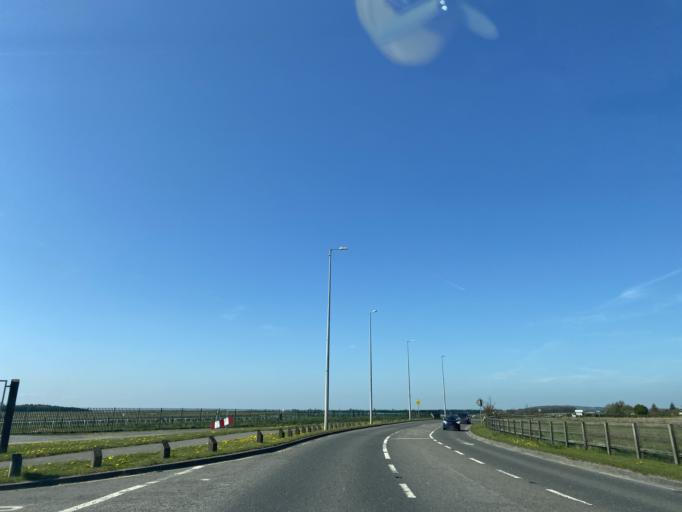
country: IE
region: Leinster
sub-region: Kildare
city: Athgarvan
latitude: 53.1693
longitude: -6.8471
